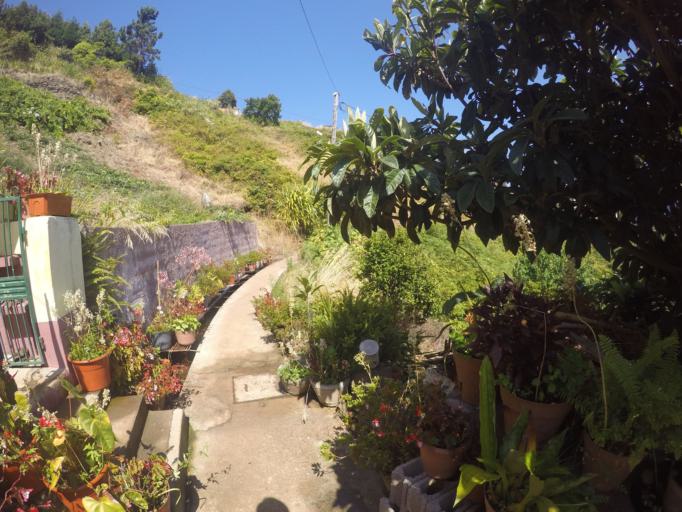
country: PT
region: Madeira
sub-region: Santana
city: Santana
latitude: 32.7564
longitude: -16.8413
